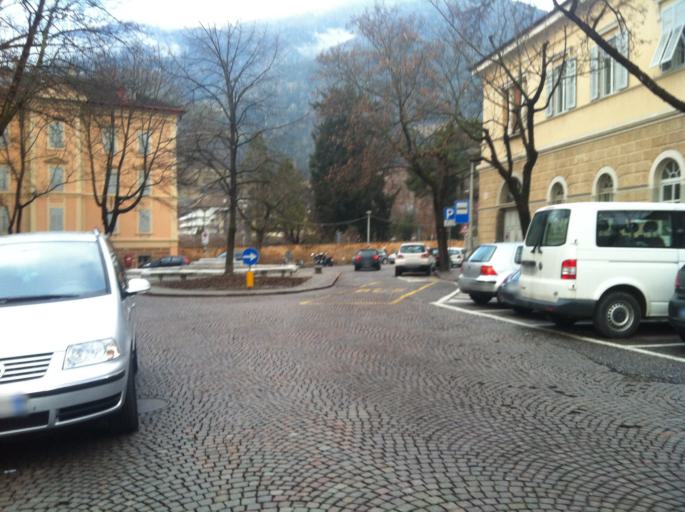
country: IT
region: Trentino-Alto Adige
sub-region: Bolzano
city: Bressanone
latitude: 46.7190
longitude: 11.6543
